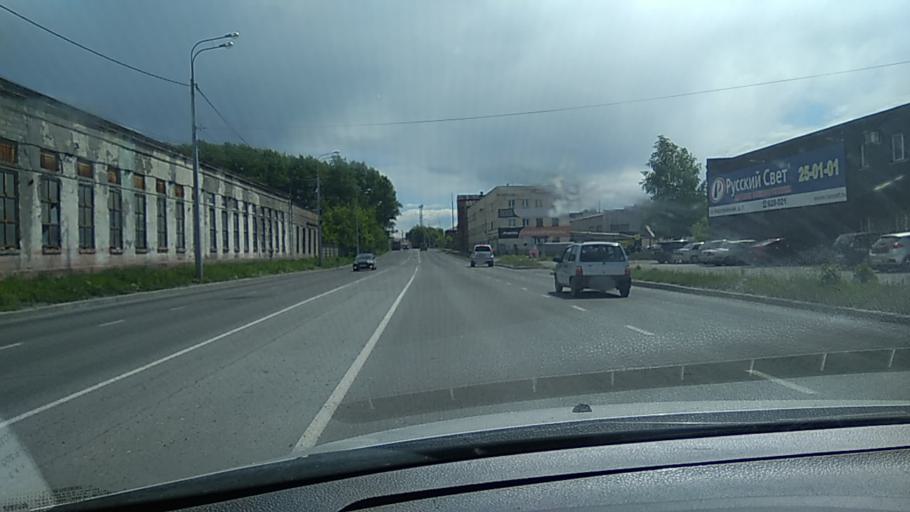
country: RU
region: Sverdlovsk
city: Nizhniy Tagil
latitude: 57.9164
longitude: 59.9900
